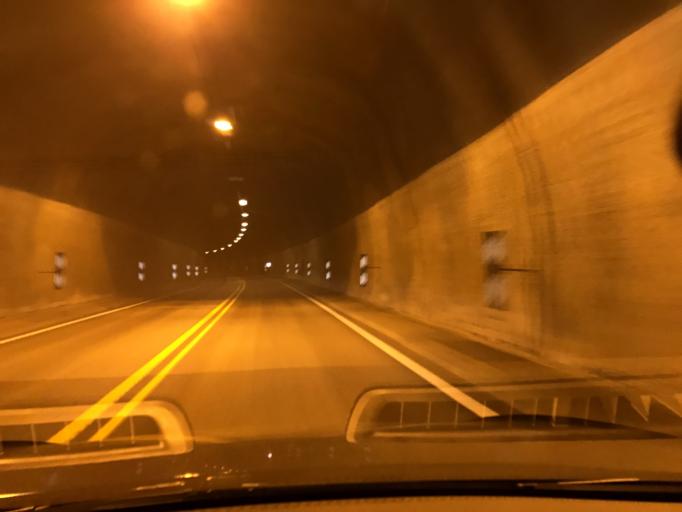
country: NO
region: Sogn og Fjordane
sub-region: Laerdal
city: Laerdalsoyri
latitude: 61.0639
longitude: 7.5015
